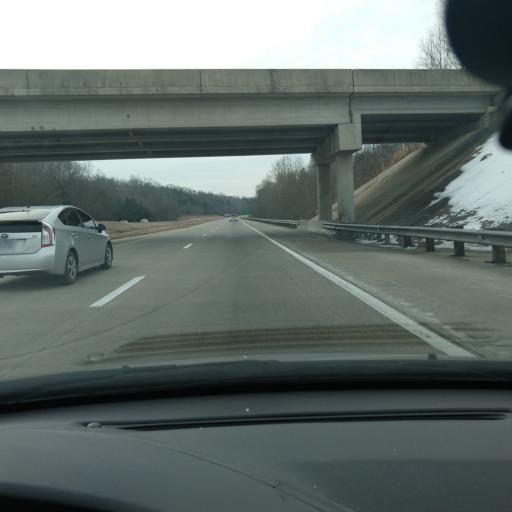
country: US
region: North Carolina
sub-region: Davidson County
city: Welcome
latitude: 35.8880
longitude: -80.2315
